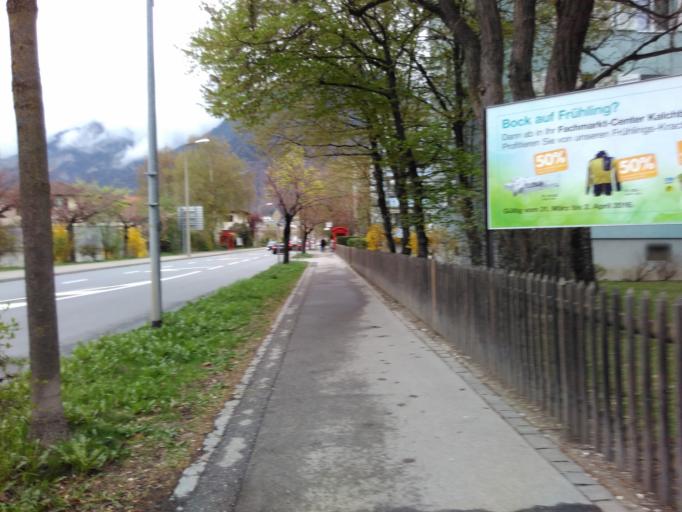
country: CH
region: Grisons
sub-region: Plessur District
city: Chur
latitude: 46.8466
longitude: 9.5154
